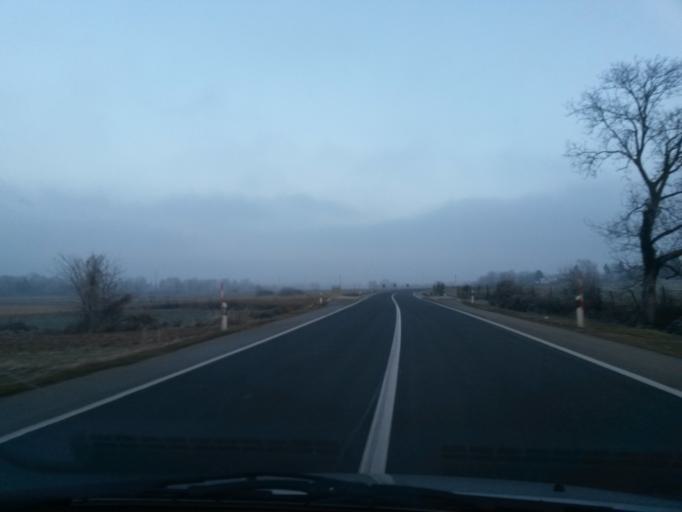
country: HR
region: Varazdinska
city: Ludbreg
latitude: 46.2145
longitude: 16.6902
